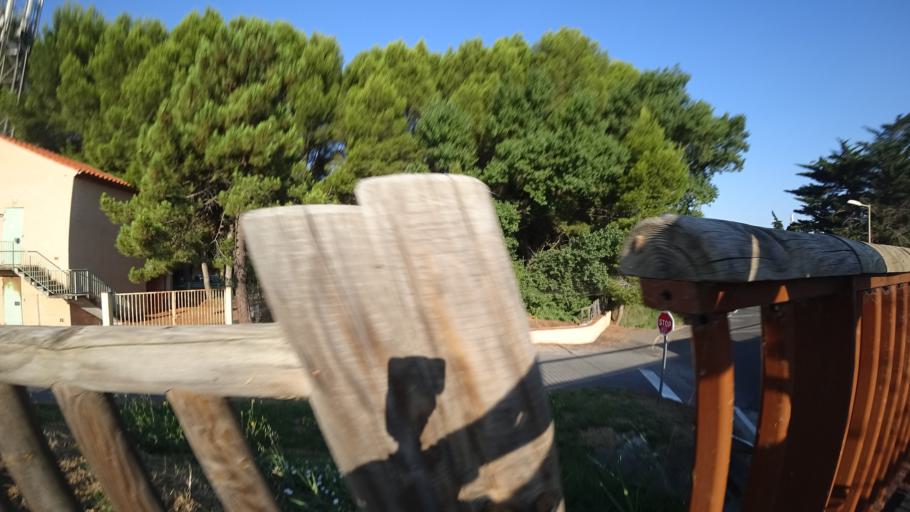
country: FR
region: Languedoc-Roussillon
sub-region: Departement des Pyrenees-Orientales
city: Sainte-Marie-Plage
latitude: 42.7292
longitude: 3.0279
